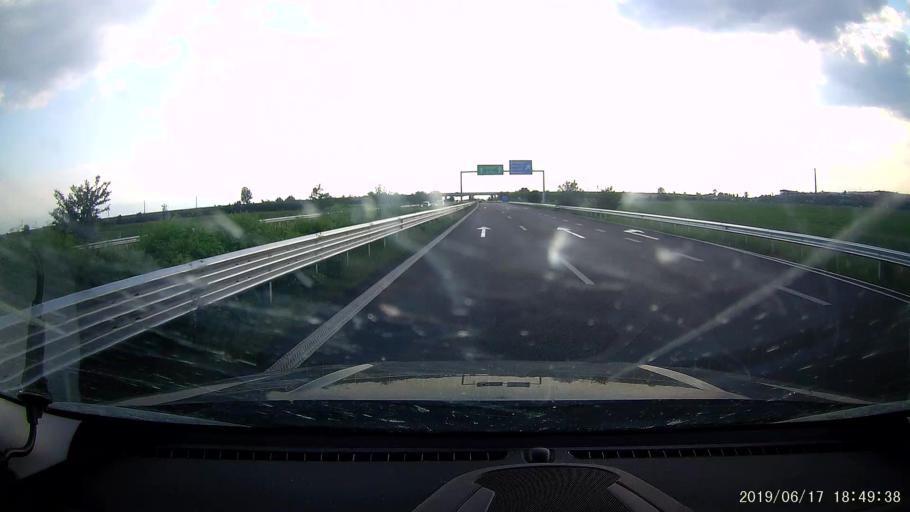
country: BG
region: Plovdiv
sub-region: Obshtina Rakovski
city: Rakovski
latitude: 42.2181
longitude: 25.0244
